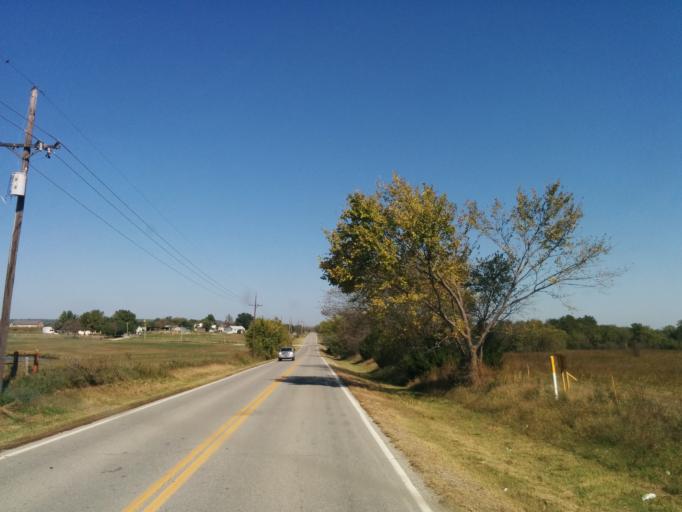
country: US
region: Oklahoma
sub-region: Creek County
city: Mounds
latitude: 35.8196
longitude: -96.0689
